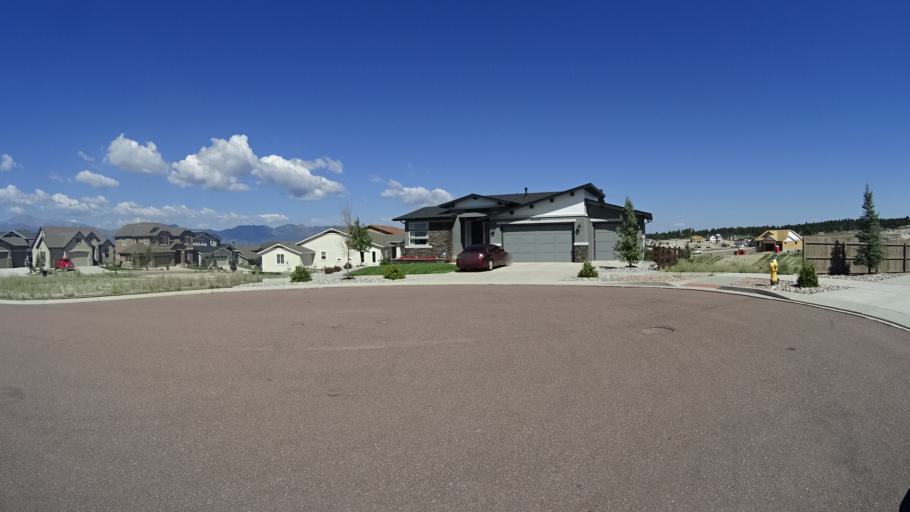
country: US
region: Colorado
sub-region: El Paso County
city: Black Forest
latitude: 38.9781
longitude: -104.7386
